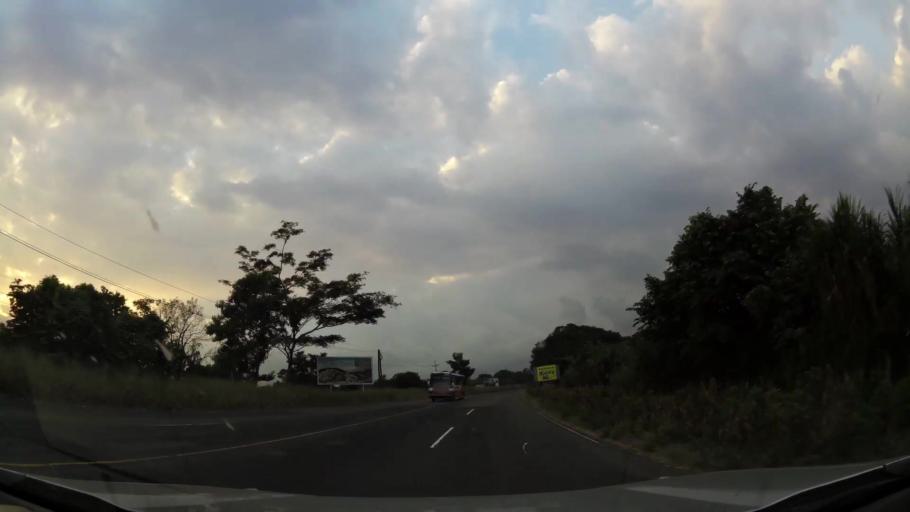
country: GT
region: Escuintla
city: Siquinala
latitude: 14.2851
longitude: -90.9366
